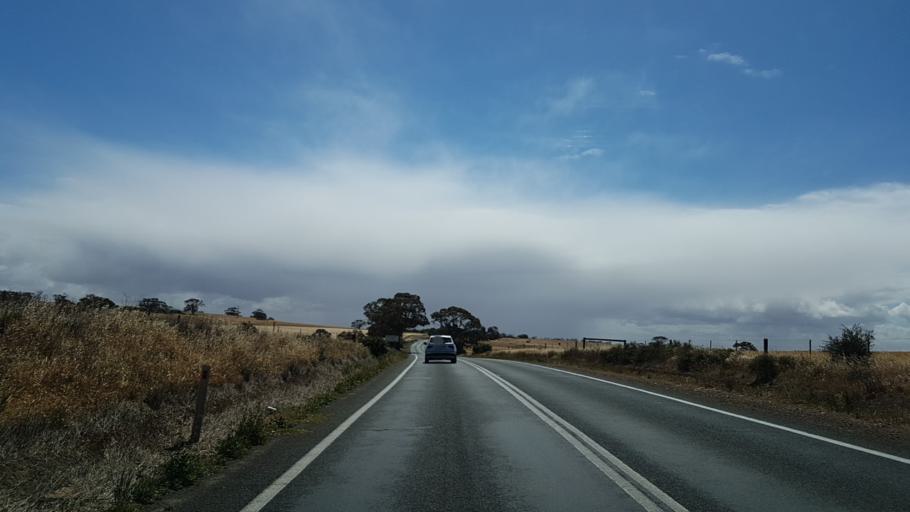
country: AU
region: South Australia
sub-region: Barossa
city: Angaston
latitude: -34.4079
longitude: 139.1385
